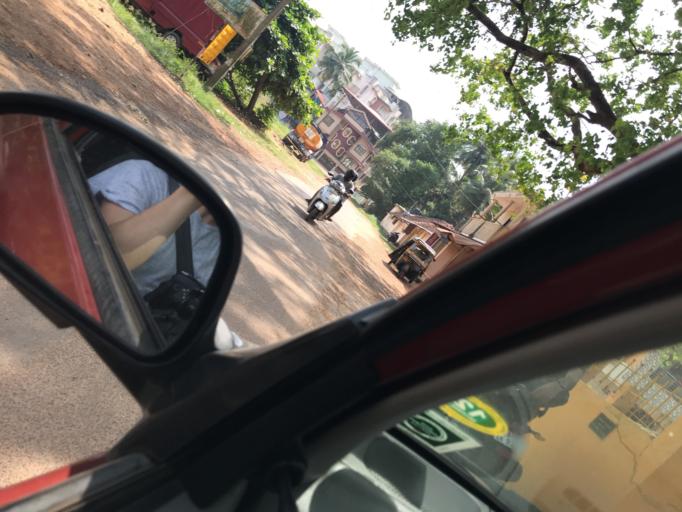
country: IN
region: Karnataka
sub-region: Dakshina Kannada
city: Ullal
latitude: 12.8470
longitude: 74.8497
